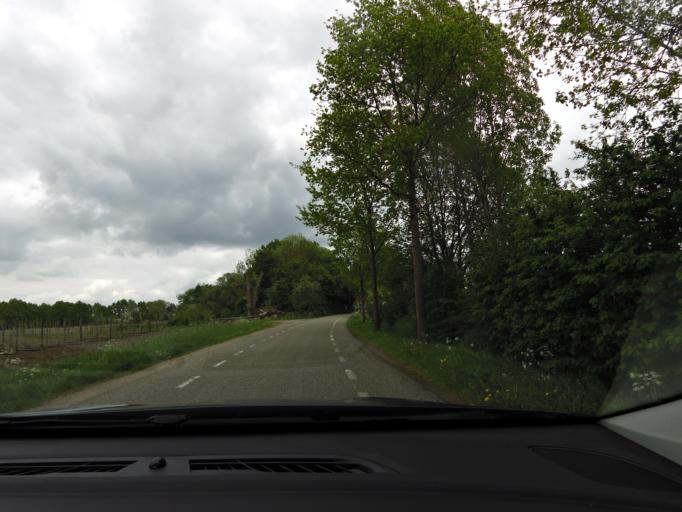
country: NL
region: Gelderland
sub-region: Gemeente Tiel
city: Tiel
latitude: 51.9173
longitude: 5.3898
